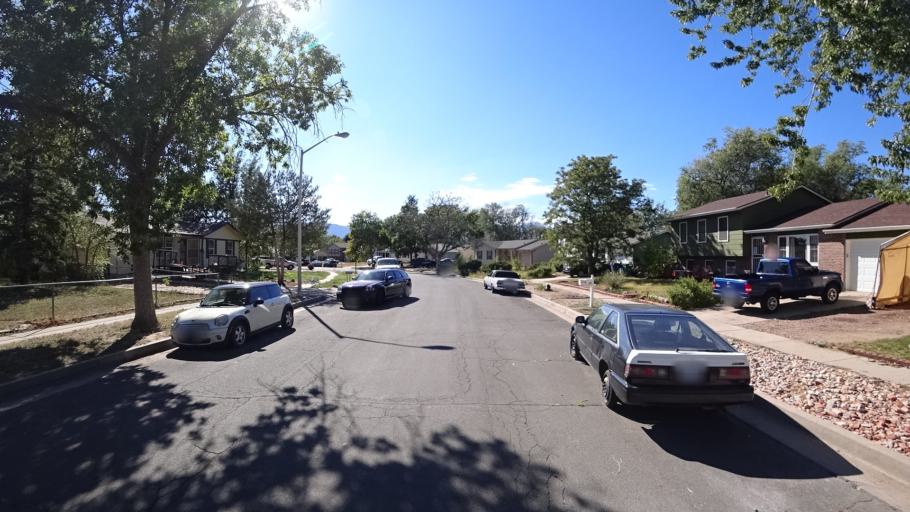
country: US
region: Colorado
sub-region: El Paso County
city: Stratmoor
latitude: 38.7982
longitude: -104.7499
